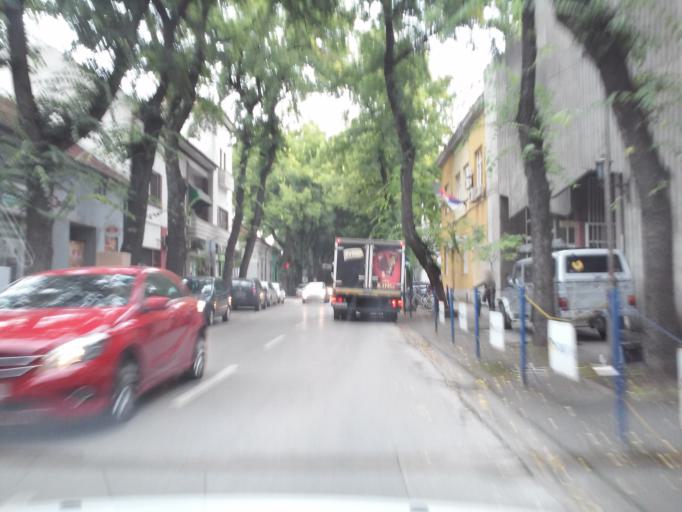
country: RS
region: Autonomna Pokrajina Vojvodina
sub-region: Severnobanatski Okrug
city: Kikinda
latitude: 45.8299
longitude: 20.4676
